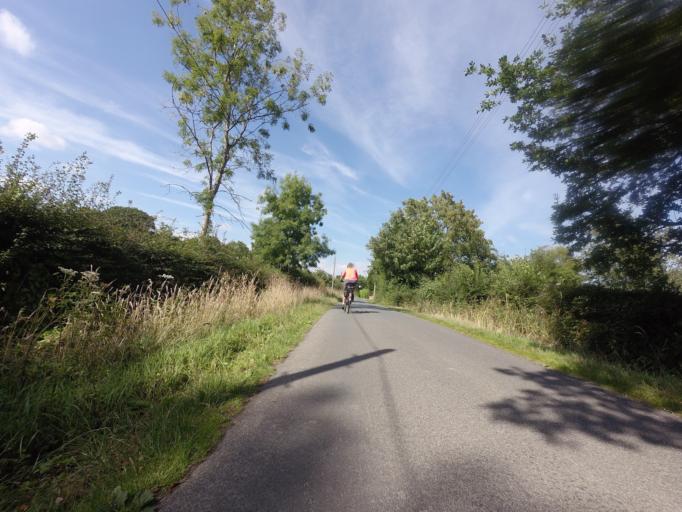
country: GB
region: England
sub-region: East Sussex
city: Rye
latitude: 50.9785
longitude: 0.7417
